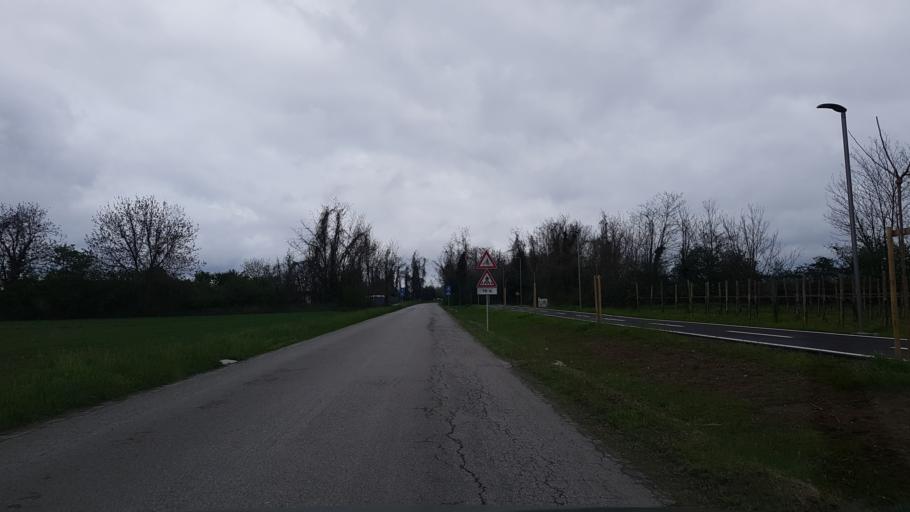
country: IT
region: Friuli Venezia Giulia
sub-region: Provincia di Gorizia
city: Turriaco
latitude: 45.8309
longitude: 13.4431
